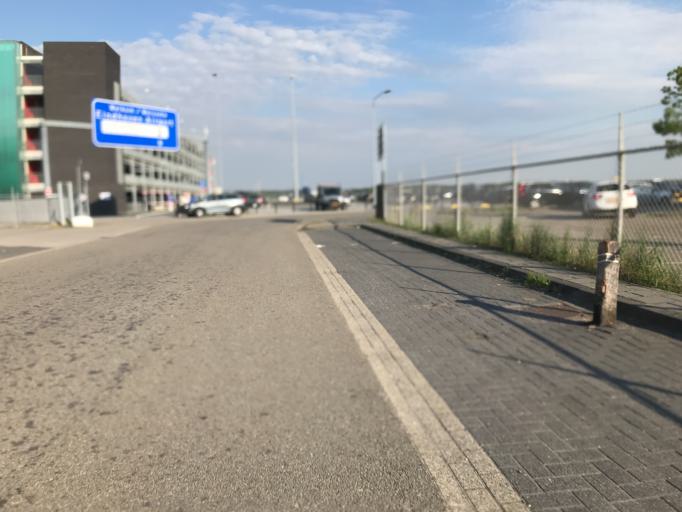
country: NL
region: North Brabant
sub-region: Gemeente Eindhoven
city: Meerhoven
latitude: 51.4540
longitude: 5.3890
